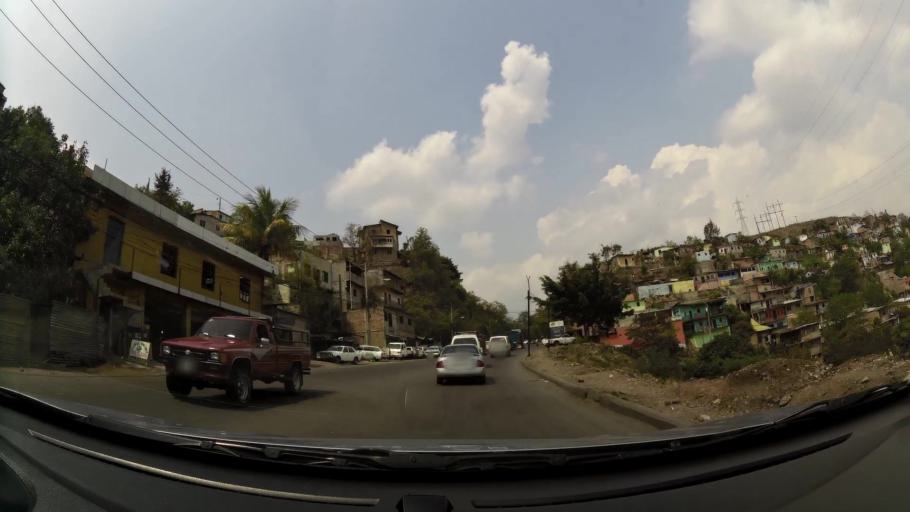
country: HN
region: Francisco Morazan
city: Tegucigalpa
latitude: 14.1128
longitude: -87.2287
